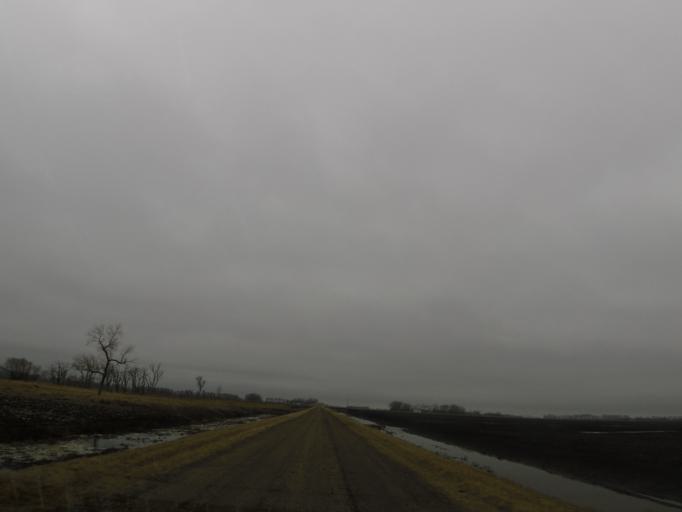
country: US
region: North Dakota
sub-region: Walsh County
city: Grafton
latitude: 48.3831
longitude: -97.1760
